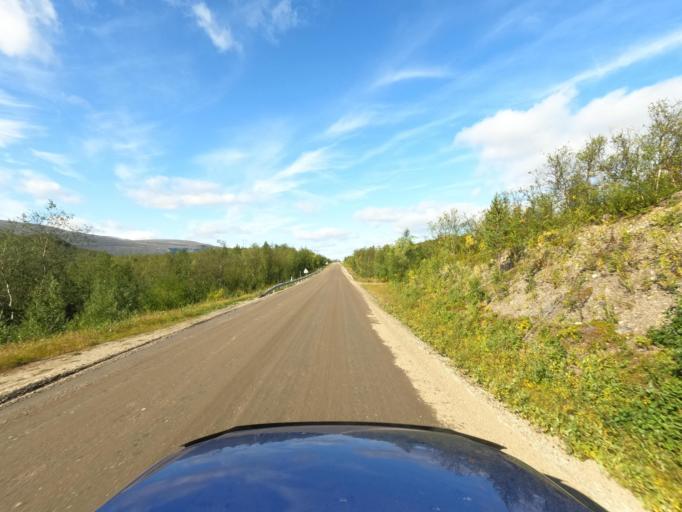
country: NO
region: Finnmark Fylke
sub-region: Porsanger
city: Lakselv
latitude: 69.8768
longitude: 25.0285
